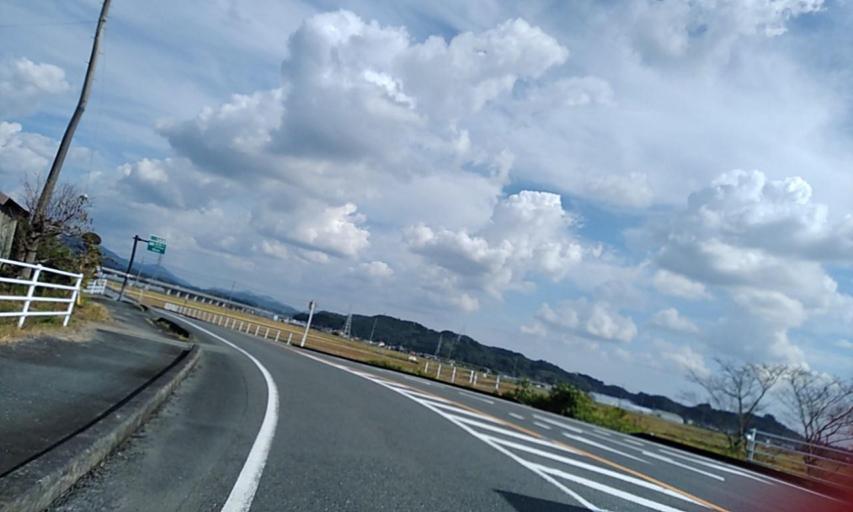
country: JP
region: Shizuoka
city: Mori
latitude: 34.8192
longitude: 137.9081
